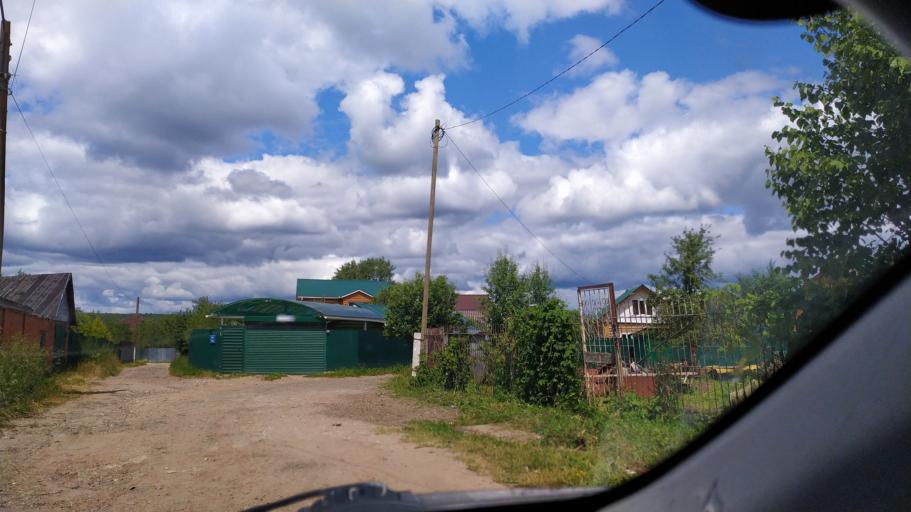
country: RU
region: Chuvashia
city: Novyye Lapsary
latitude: 56.1126
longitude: 47.1754
